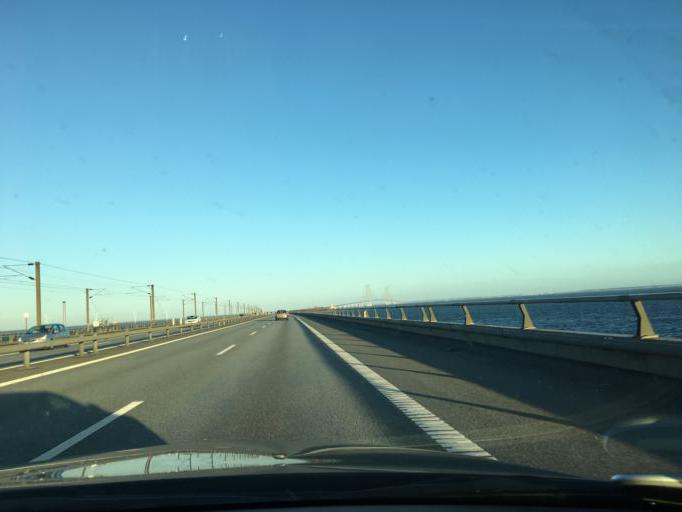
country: DK
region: South Denmark
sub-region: Nyborg Kommune
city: Nyborg
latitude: 55.3167
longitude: 10.9228
